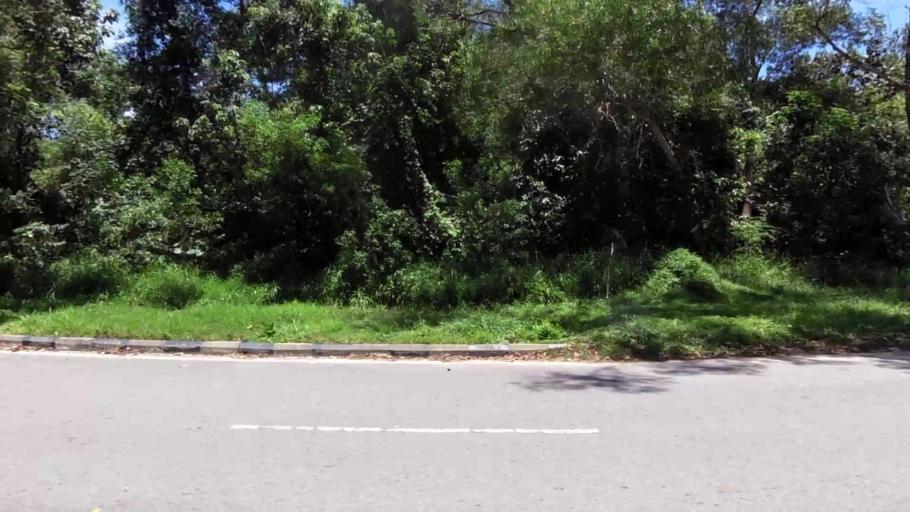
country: BN
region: Brunei and Muara
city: Bandar Seri Begawan
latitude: 4.9229
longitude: 114.9573
